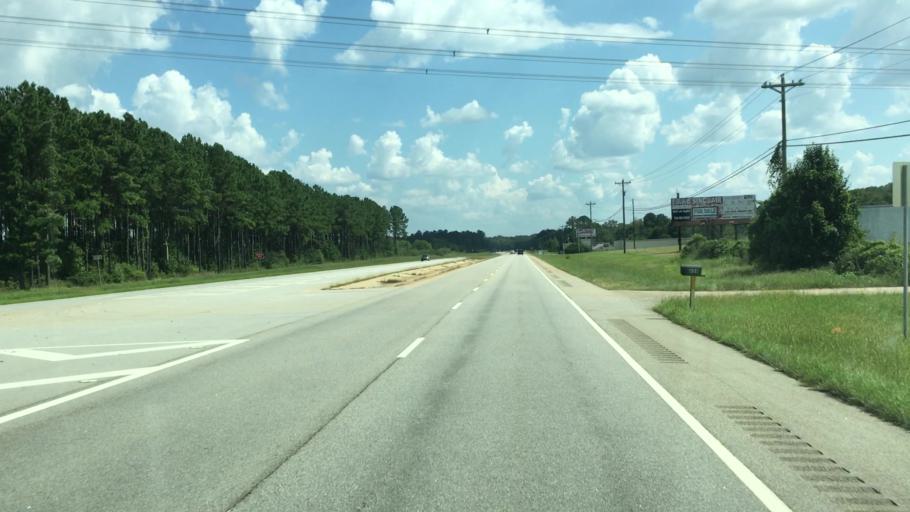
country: US
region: Georgia
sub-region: Putnam County
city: Eatonton
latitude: 33.2539
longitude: -83.3290
